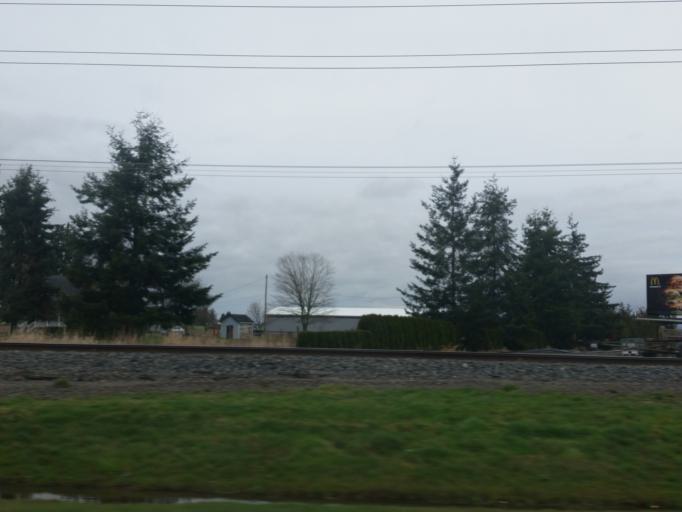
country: US
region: Washington
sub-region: Skagit County
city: Burlington
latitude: 48.4643
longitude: -122.3616
